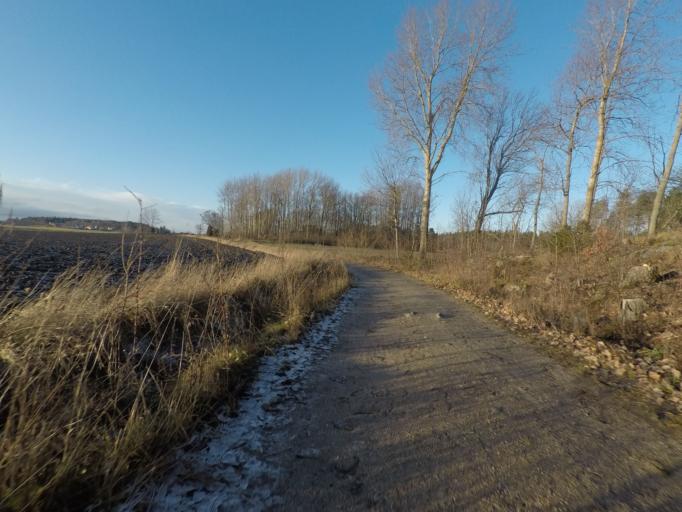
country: SE
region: Soedermanland
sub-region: Eskilstuna Kommun
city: Eskilstuna
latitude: 59.4012
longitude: 16.5244
